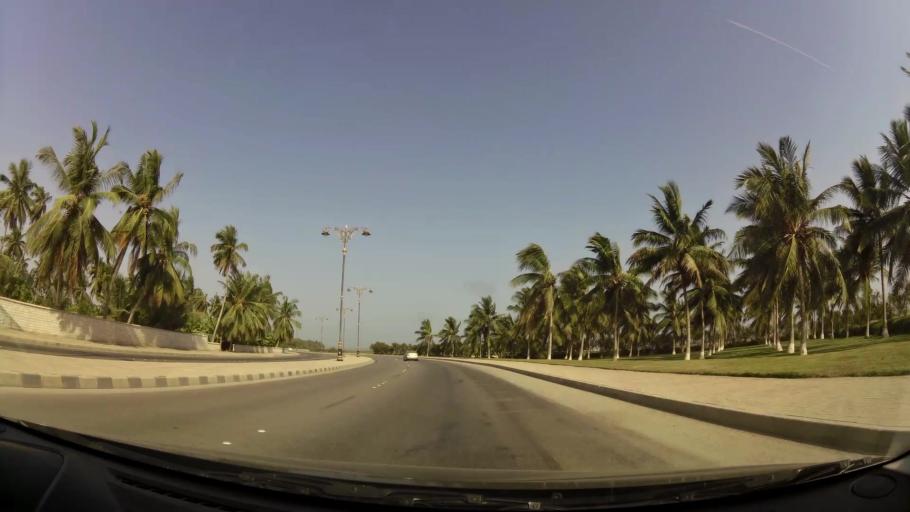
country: OM
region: Zufar
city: Salalah
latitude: 16.9990
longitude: 54.0708
